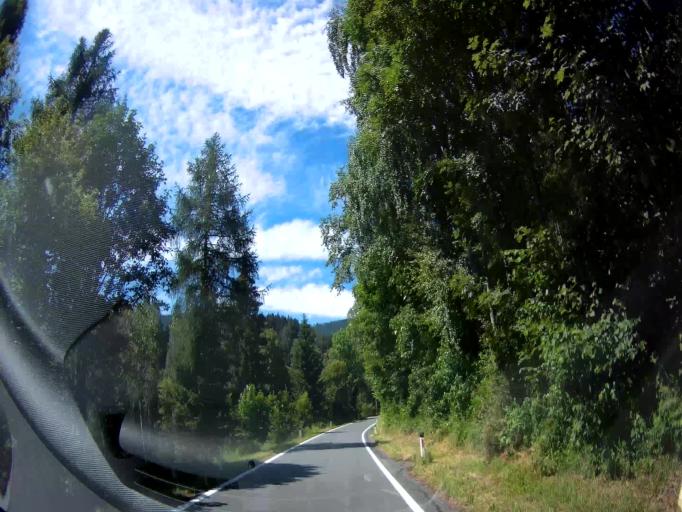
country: AT
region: Carinthia
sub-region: Politischer Bezirk Sankt Veit an der Glan
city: Glodnitz
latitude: 46.9168
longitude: 14.0860
